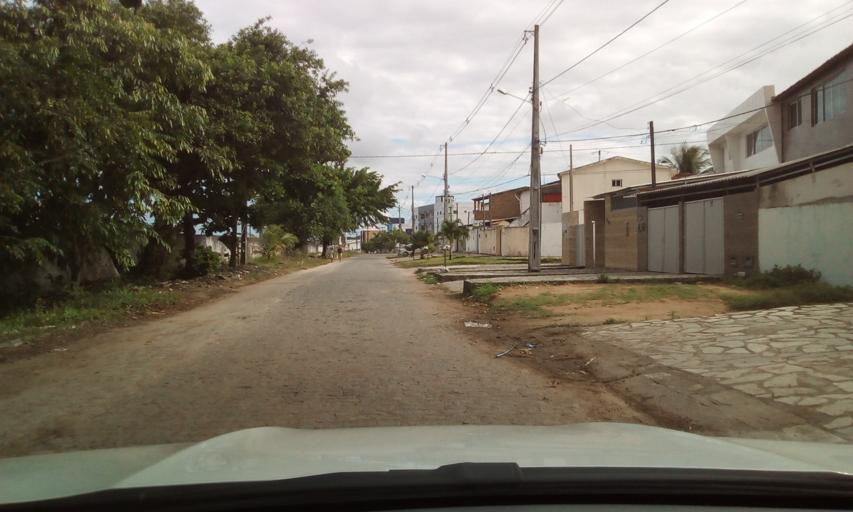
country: BR
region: Paraiba
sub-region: Joao Pessoa
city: Joao Pessoa
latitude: -7.1841
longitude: -34.8794
